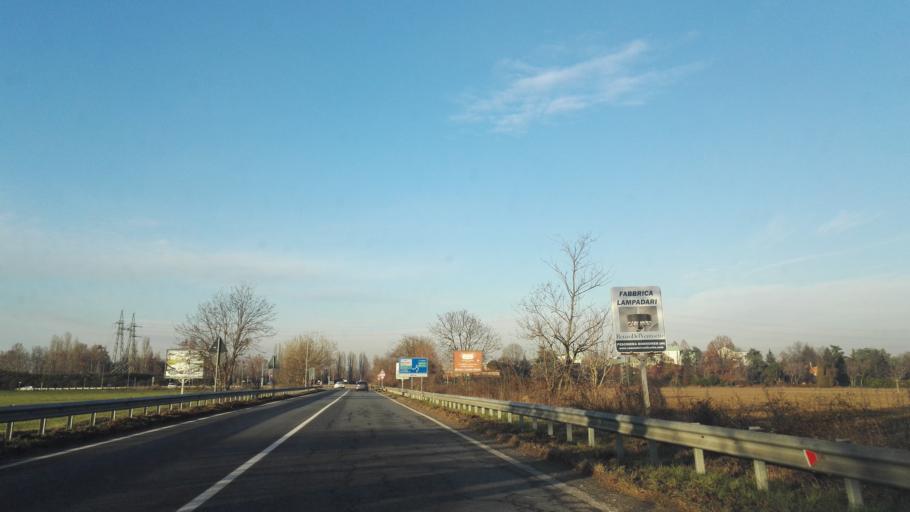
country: IT
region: Lombardy
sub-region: Citta metropolitana di Milano
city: San Bovio-San Felice
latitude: 45.4636
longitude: 9.3031
